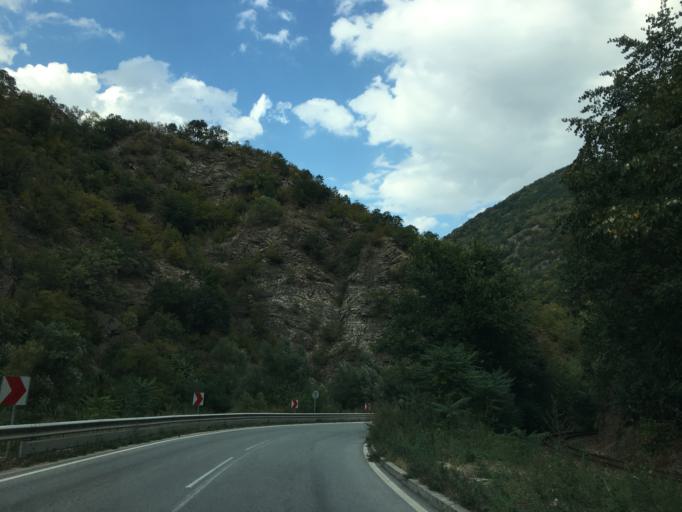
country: BG
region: Pazardzhik
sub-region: Obshtina Septemvri
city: Septemvri
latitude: 42.1279
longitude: 24.1231
